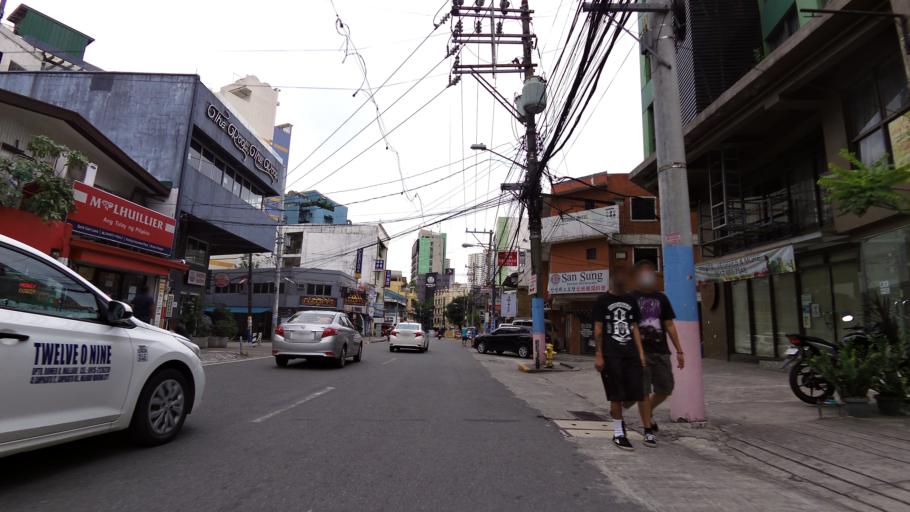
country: PH
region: Metro Manila
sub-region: Makati City
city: Makati City
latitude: 14.5649
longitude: 121.0312
